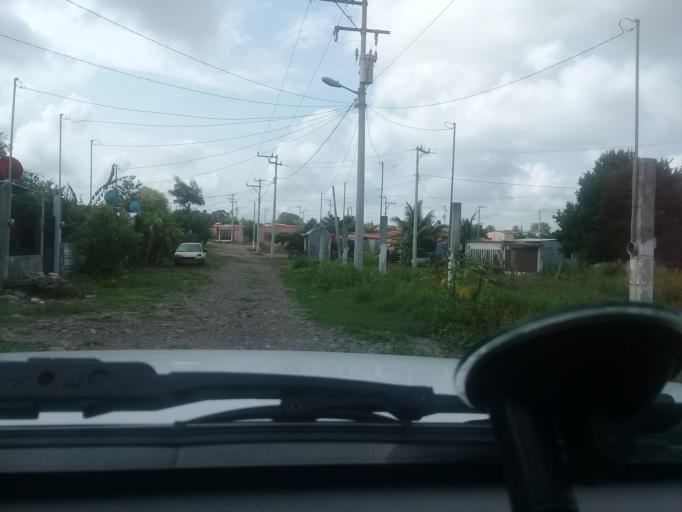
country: MX
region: Veracruz
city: Paso de Ovejas
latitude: 19.2715
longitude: -96.4192
